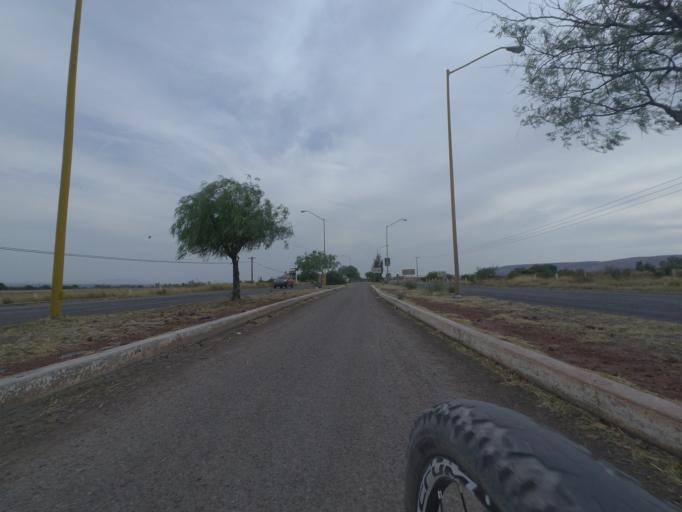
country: MX
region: Aguascalientes
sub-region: Aguascalientes
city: La Loma de los Negritos
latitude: 21.8710
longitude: -102.3707
